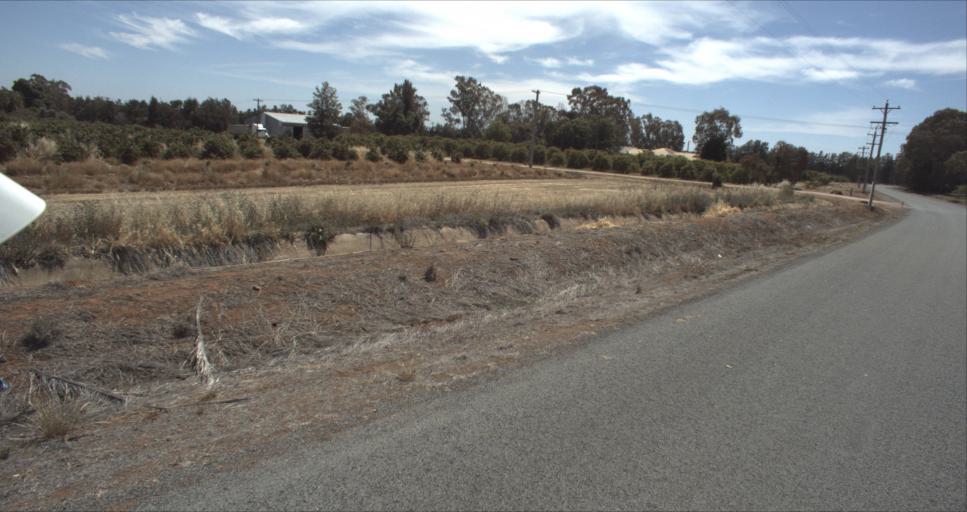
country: AU
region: New South Wales
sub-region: Leeton
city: Leeton
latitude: -34.5753
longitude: 146.4311
